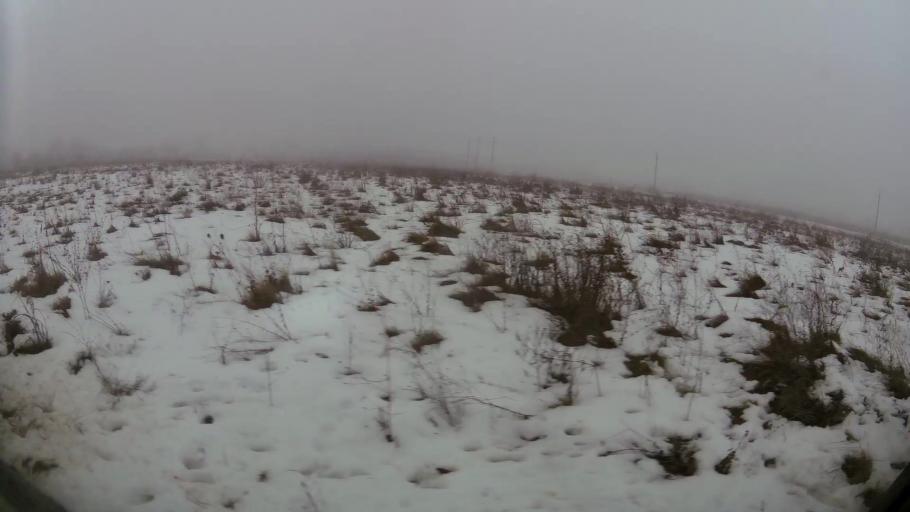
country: RO
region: Ilfov
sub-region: Comuna Chiajna
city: Chiajna
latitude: 44.4506
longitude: 25.9679
